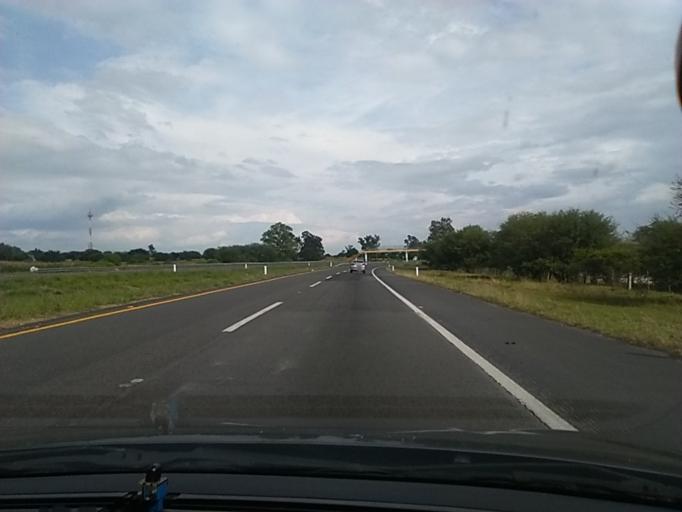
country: MX
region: Jalisco
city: La Barca
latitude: 20.3342
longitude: -102.5923
